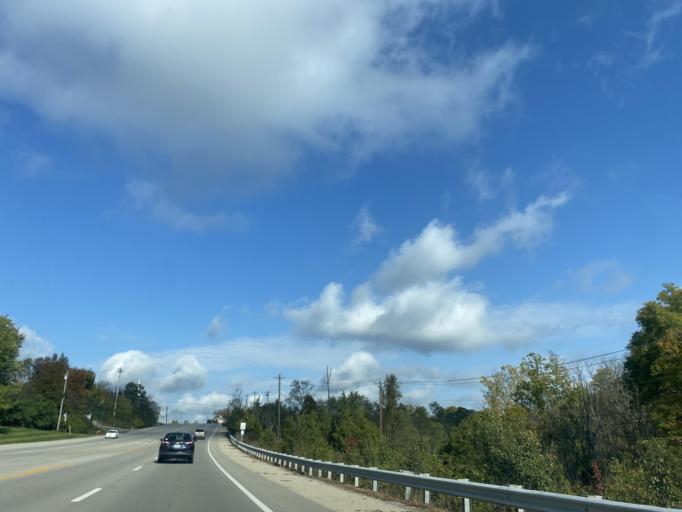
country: US
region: Kentucky
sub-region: Campbell County
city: Cold Spring
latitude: 39.0123
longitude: -84.4318
